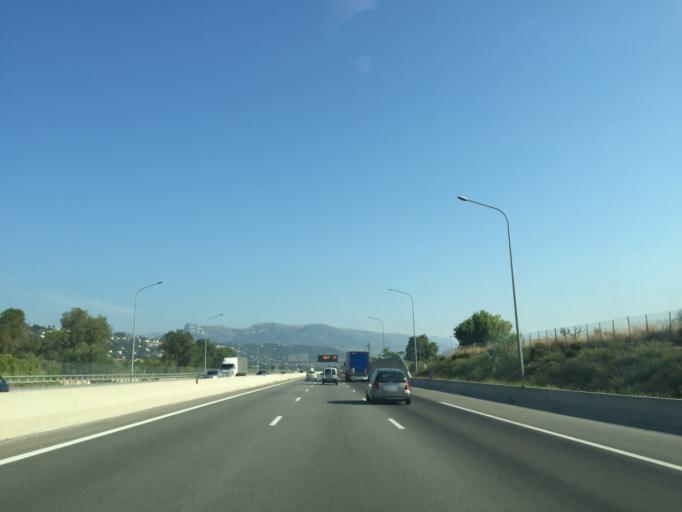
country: FR
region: Provence-Alpes-Cote d'Azur
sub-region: Departement des Alpes-Maritimes
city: Saint-Laurent-du-Var
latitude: 43.6800
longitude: 7.1937
